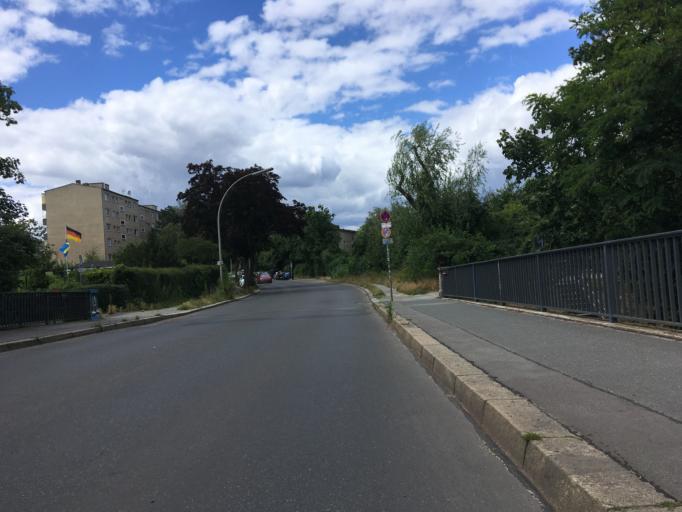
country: DE
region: Berlin
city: Mariendorf
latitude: 52.4484
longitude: 13.3698
